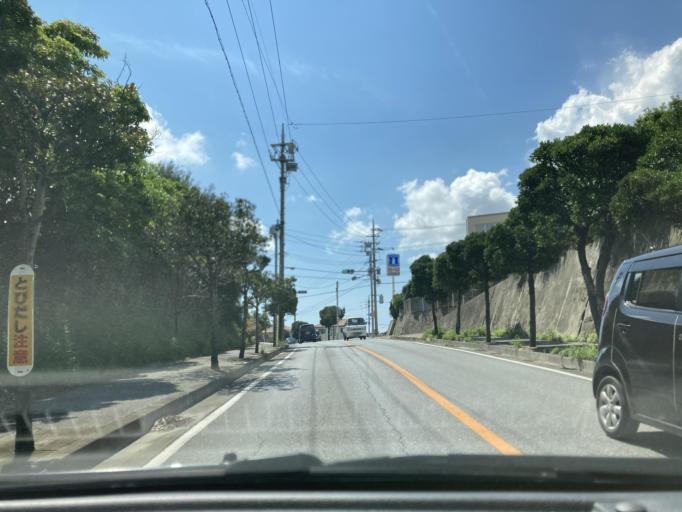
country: JP
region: Okinawa
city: Tomigusuku
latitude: 26.1665
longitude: 127.7546
